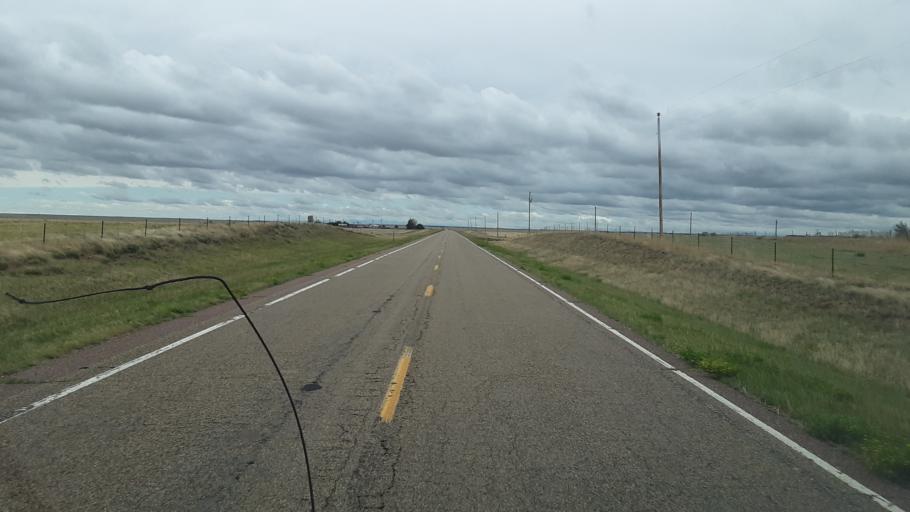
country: US
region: Colorado
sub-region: Lincoln County
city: Limon
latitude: 38.8387
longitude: -103.8809
